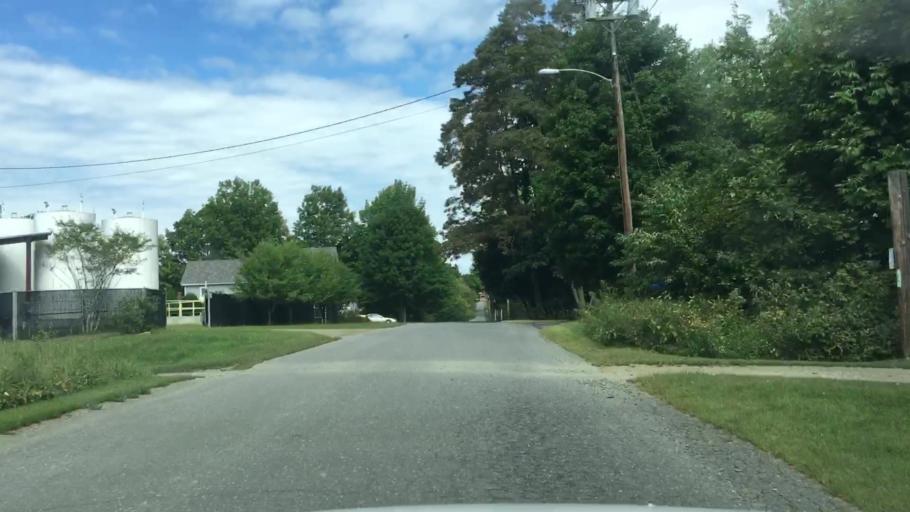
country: US
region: Maine
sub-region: Piscataquis County
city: Dover-Foxcroft
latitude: 45.1864
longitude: -69.2219
